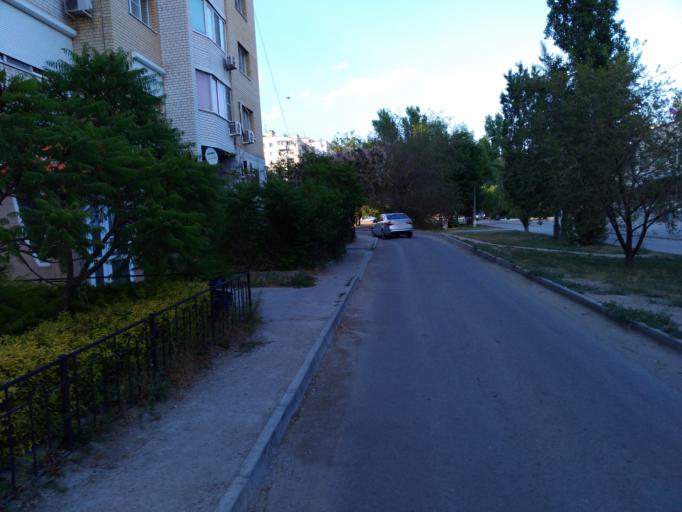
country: RU
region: Volgograd
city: Volgograd
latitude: 48.7203
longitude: 44.5117
